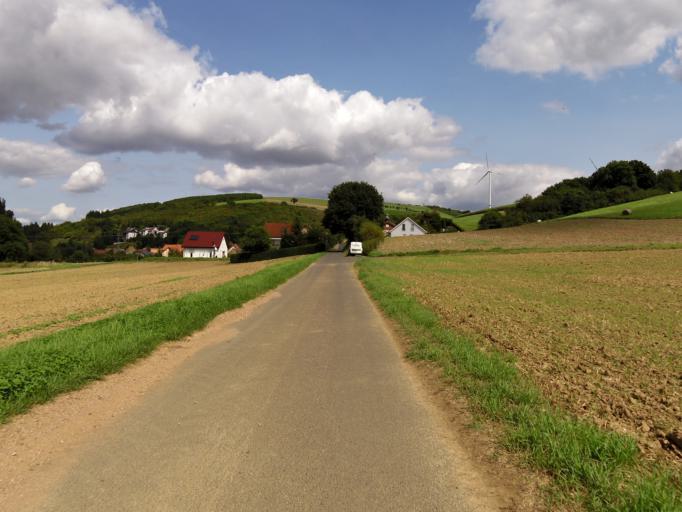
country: DE
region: Rheinland-Pfalz
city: Niederhausen an der Appel
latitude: 49.7433
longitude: 7.8913
